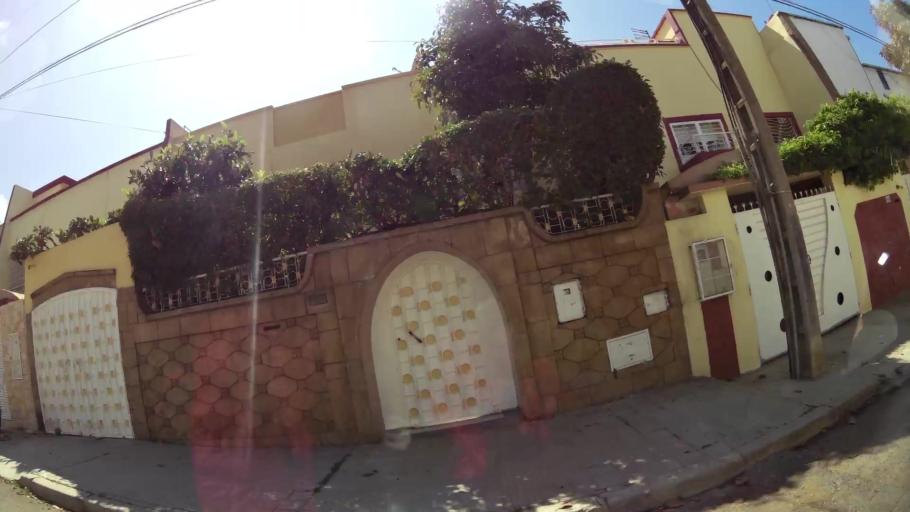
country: MA
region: Rabat-Sale-Zemmour-Zaer
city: Sale
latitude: 34.0424
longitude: -6.7865
